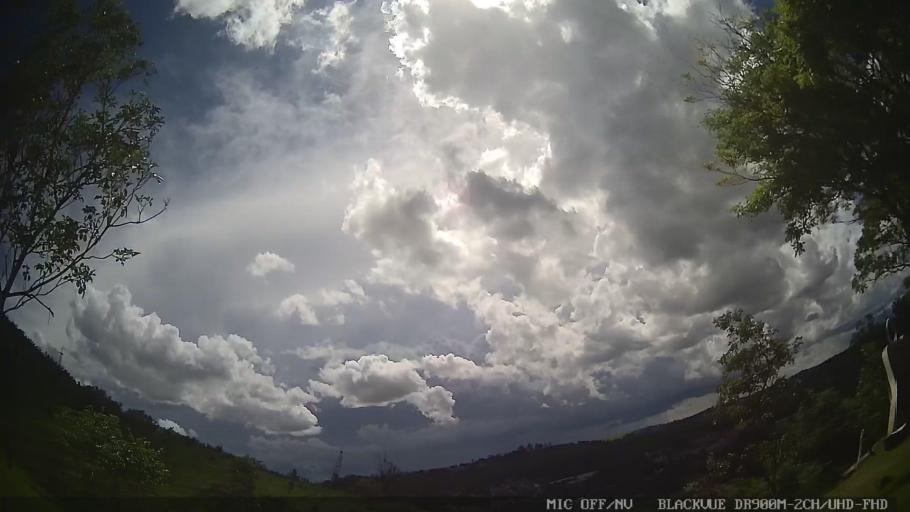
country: BR
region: Sao Paulo
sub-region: Pedreira
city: Pedreira
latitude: -22.7449
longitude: -46.9085
